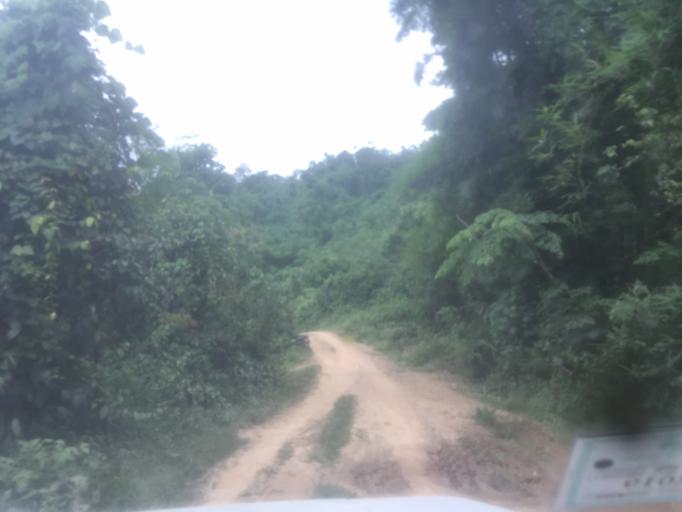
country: LA
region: Phongsali
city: Khoa
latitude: 20.9102
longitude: 102.5524
